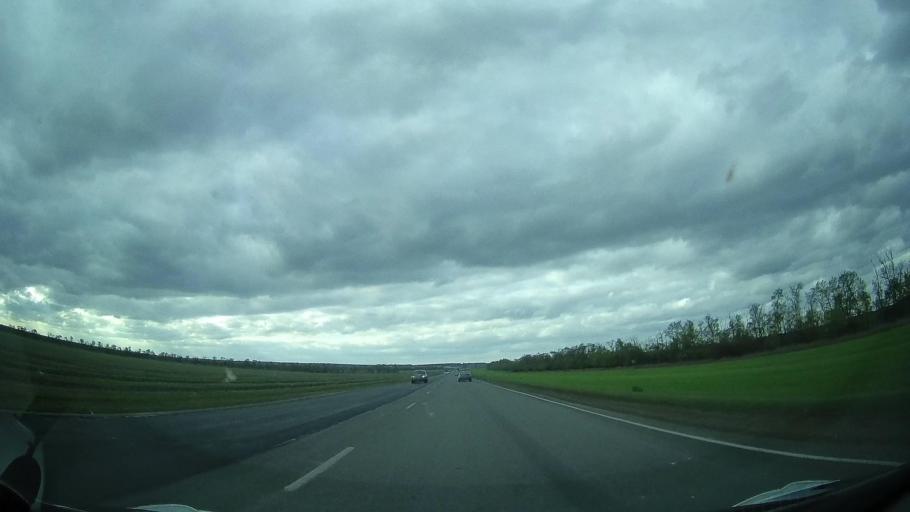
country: RU
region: Rostov
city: Kagal'nitskaya
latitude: 46.8658
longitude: 40.1763
